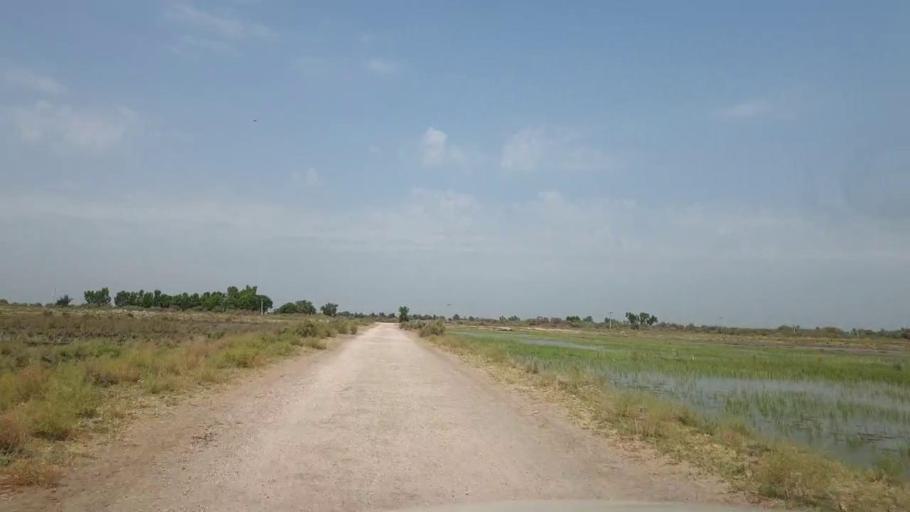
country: PK
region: Sindh
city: Ratodero
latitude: 27.8393
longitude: 68.2509
